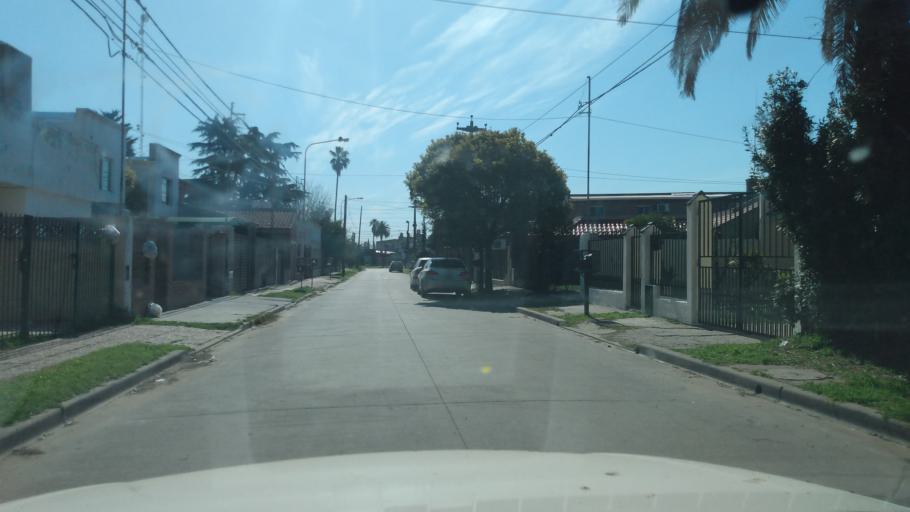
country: AR
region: Buenos Aires
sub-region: Partido de Lujan
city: Lujan
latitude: -34.5793
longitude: -59.1010
